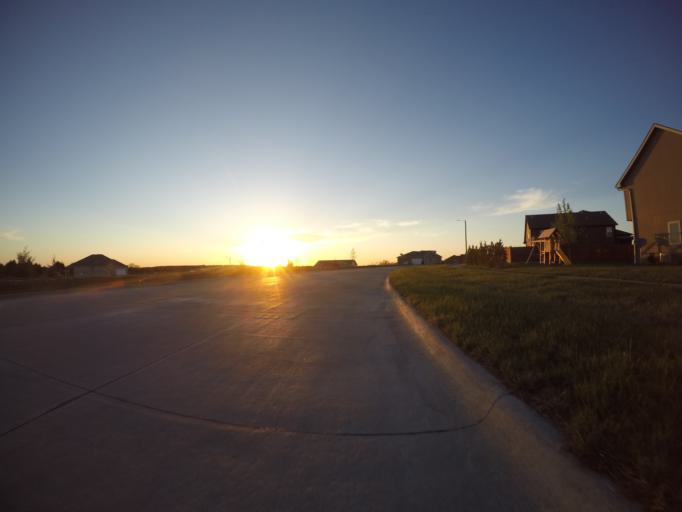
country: US
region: Kansas
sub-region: Riley County
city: Manhattan
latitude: 39.1717
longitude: -96.6337
